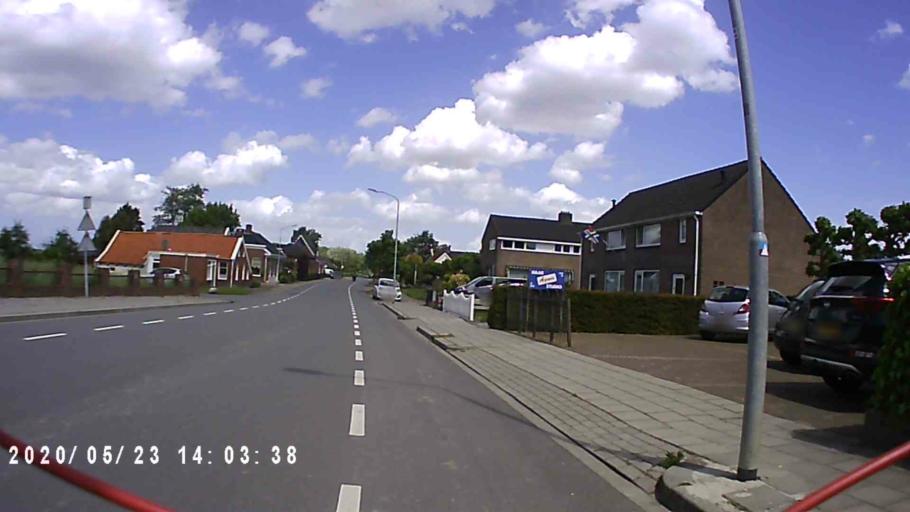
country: NL
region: Groningen
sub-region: Gemeente Delfzijl
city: Delfzijl
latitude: 53.2749
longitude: 7.0308
